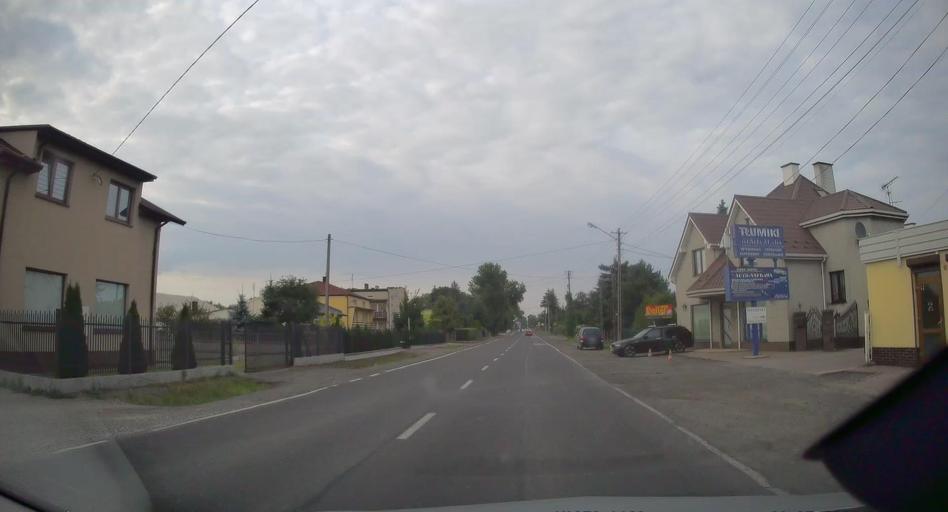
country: PL
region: Lodz Voivodeship
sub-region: Powiat radomszczanski
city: Radomsko
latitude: 51.0948
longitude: 19.4589
